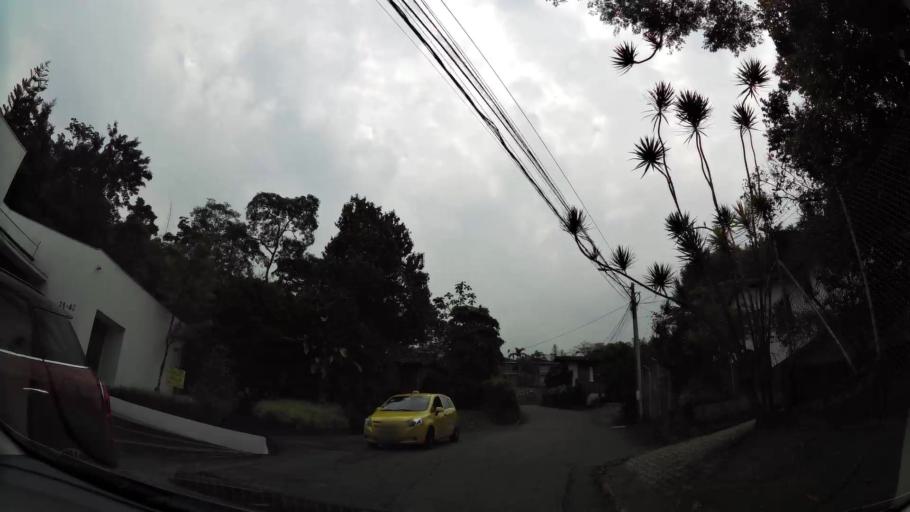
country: CO
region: Antioquia
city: Medellin
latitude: 6.2103
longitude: -75.5577
